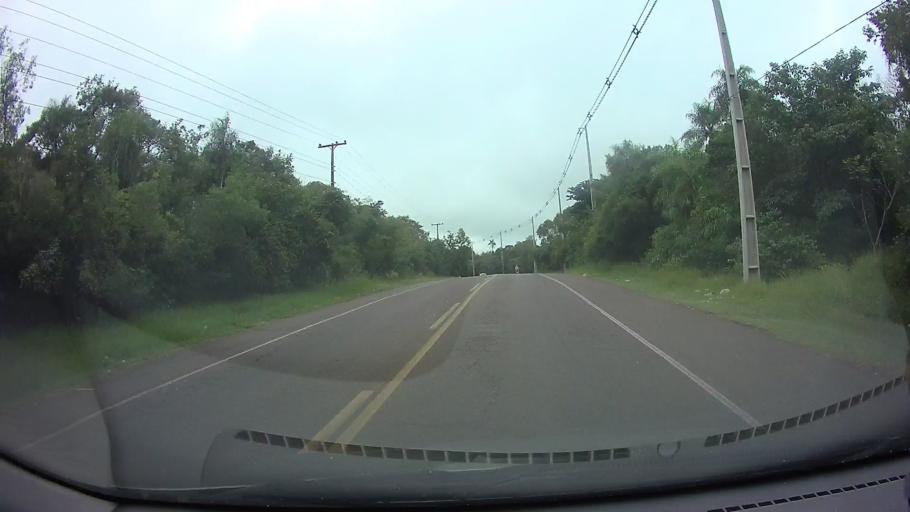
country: PY
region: Cordillera
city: Altos
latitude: -25.2812
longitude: -57.2619
